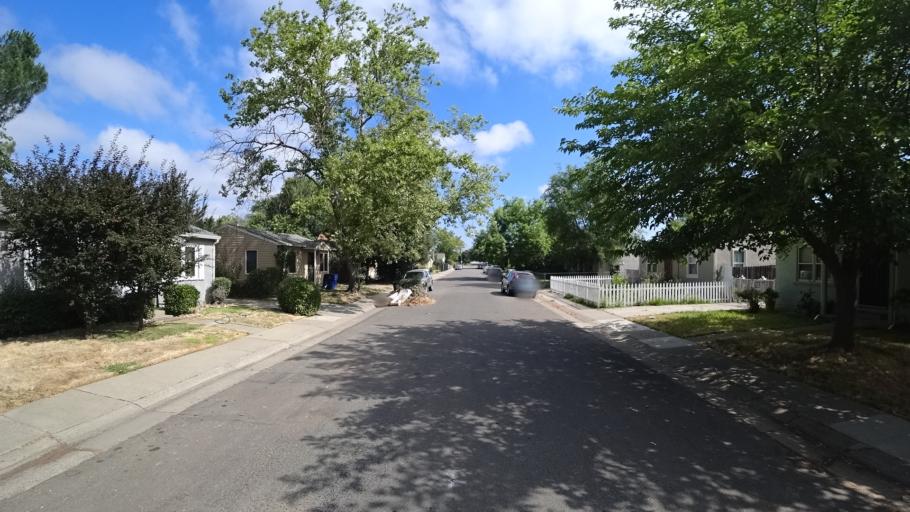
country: US
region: California
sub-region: Sacramento County
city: Sacramento
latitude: 38.5357
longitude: -121.4855
